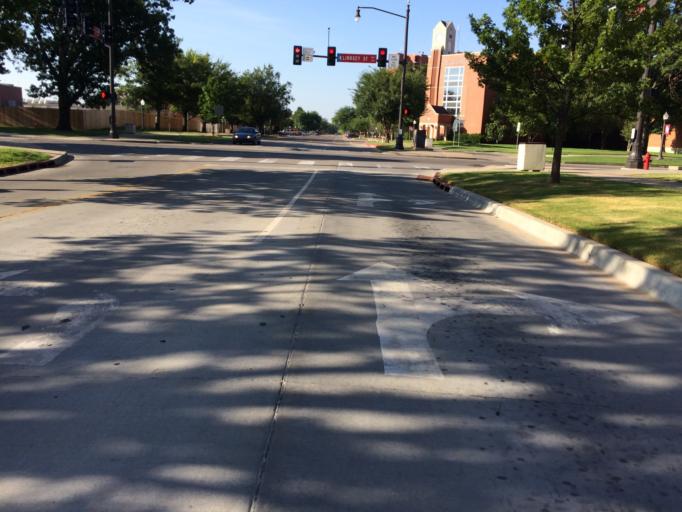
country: US
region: Oklahoma
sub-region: Cleveland County
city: Norman
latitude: 35.2042
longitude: -97.4443
